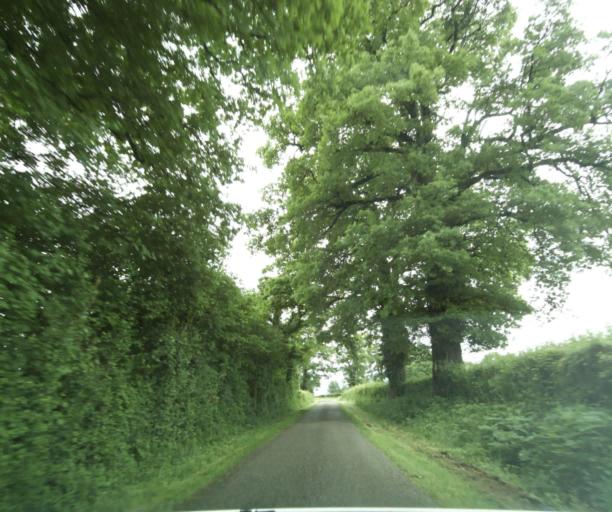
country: FR
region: Bourgogne
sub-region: Departement de Saone-et-Loire
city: Charolles
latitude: 46.4574
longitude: 4.2900
